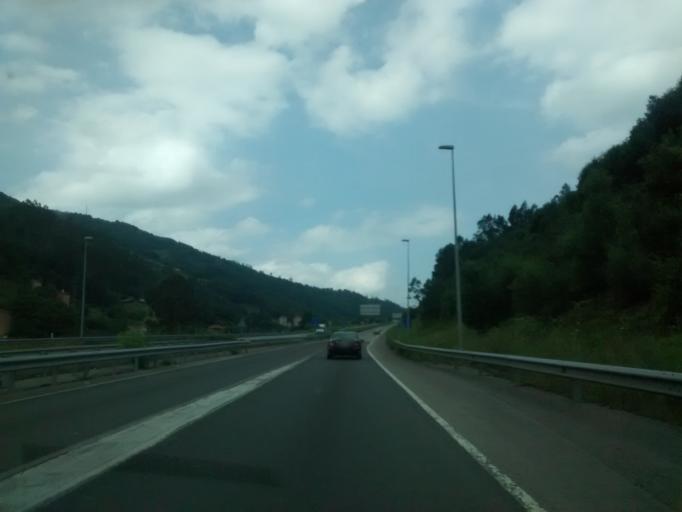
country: ES
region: Asturias
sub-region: Province of Asturias
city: Mieres
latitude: 43.2633
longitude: -5.7791
